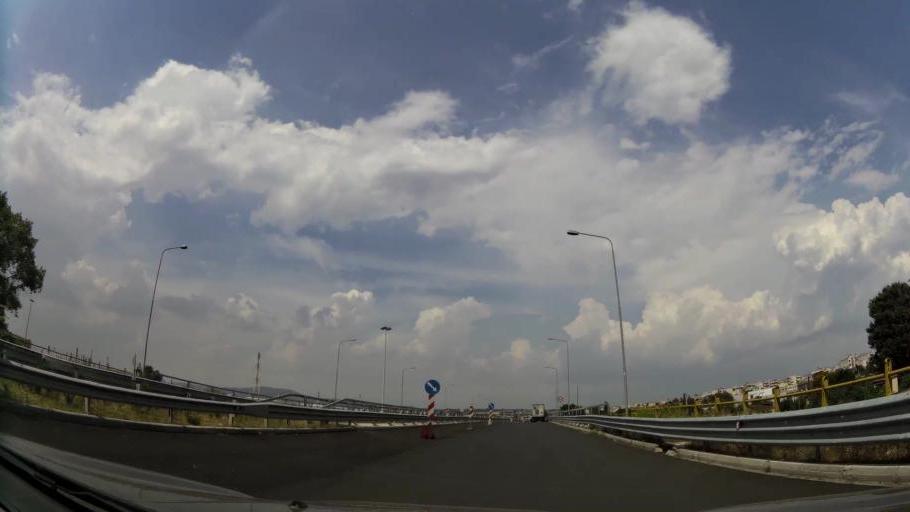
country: GR
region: Central Macedonia
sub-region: Nomos Thessalonikis
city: Menemeni
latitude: 40.6688
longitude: 22.8840
